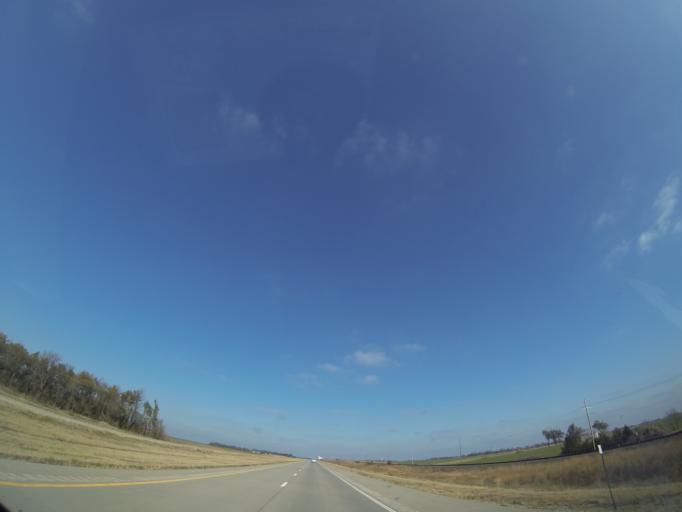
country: US
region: Kansas
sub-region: McPherson County
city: Inman
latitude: 38.2016
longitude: -97.8012
